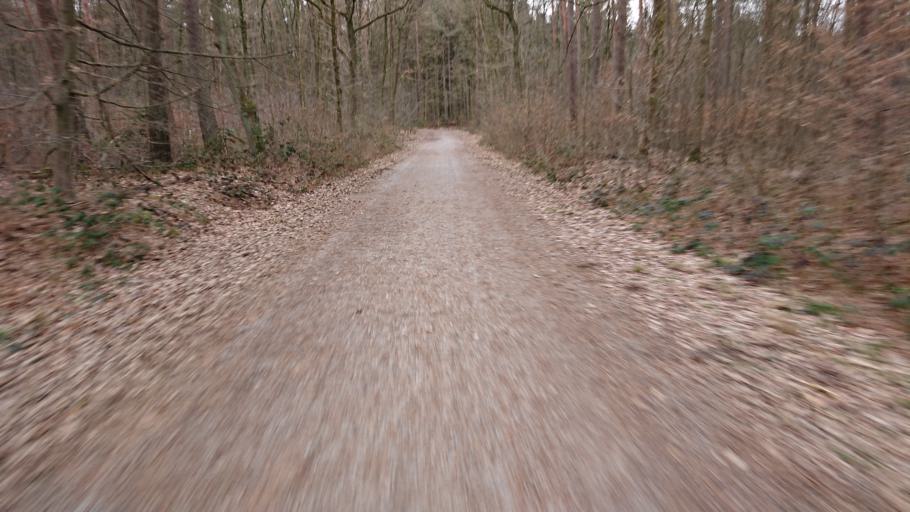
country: DE
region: North Rhine-Westphalia
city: Opladen
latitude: 51.0082
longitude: 7.0455
